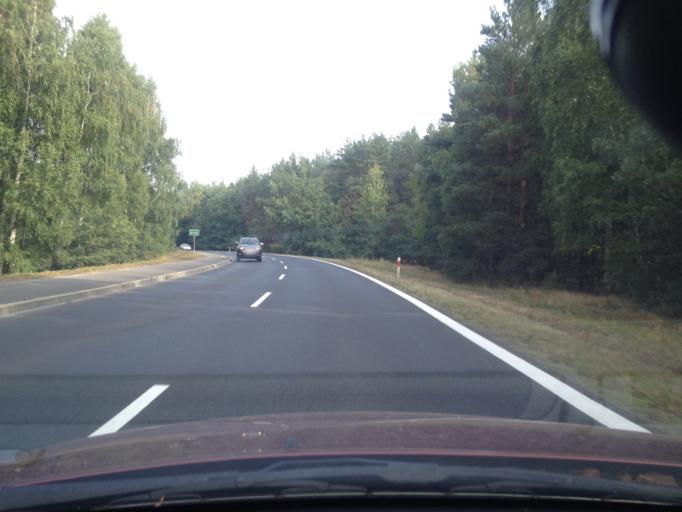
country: PL
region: Lubusz
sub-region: Powiat zaganski
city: Szprotawa
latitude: 51.4394
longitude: 15.6010
